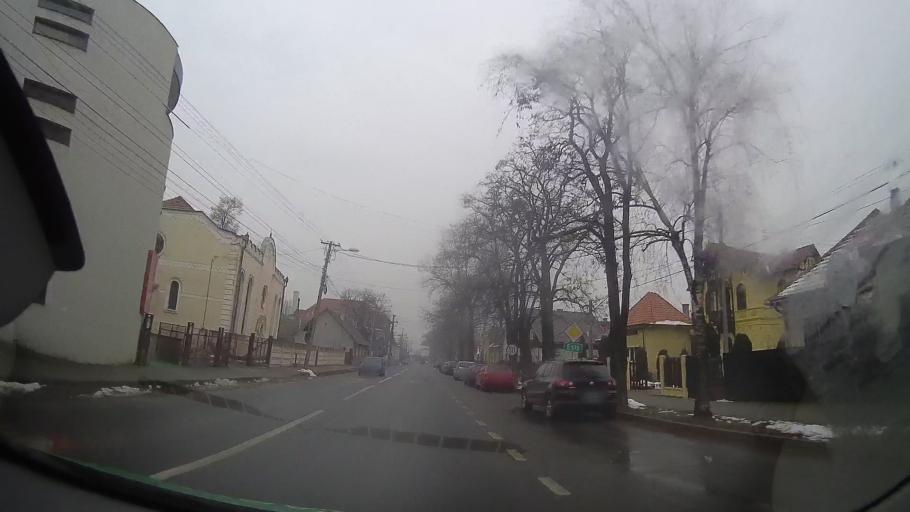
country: RO
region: Harghita
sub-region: Municipiul Gheorgheni
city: Gheorgheni
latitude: 46.7233
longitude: 25.5976
